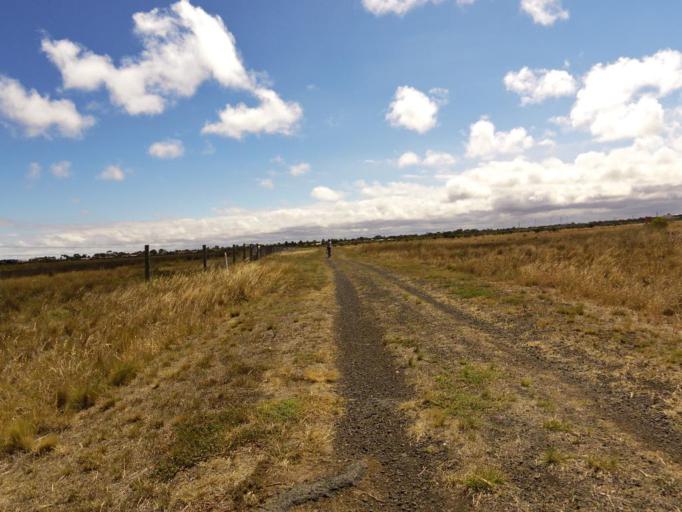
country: AU
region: Victoria
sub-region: Hobsons Bay
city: Altona Meadows
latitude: -37.8648
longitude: 144.8006
